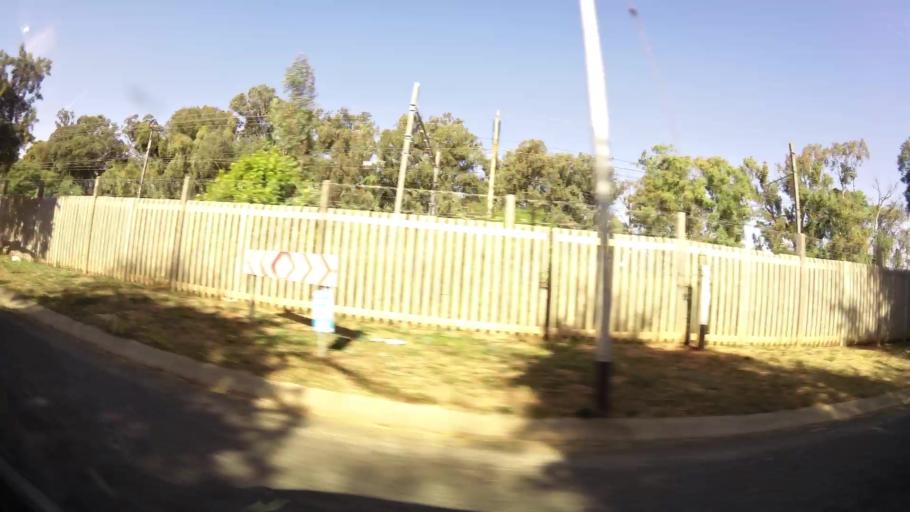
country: ZA
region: Gauteng
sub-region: City of Tshwane Metropolitan Municipality
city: Pretoria
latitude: -25.7305
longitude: 28.2674
